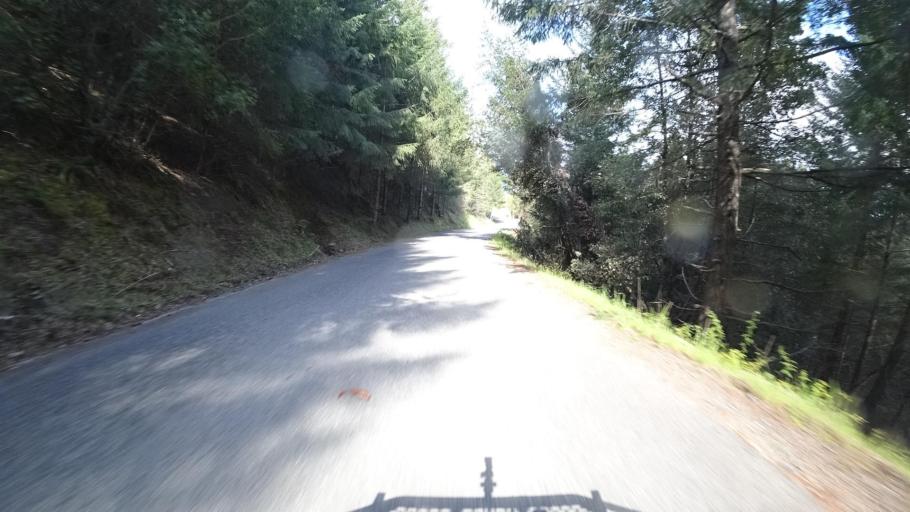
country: US
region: California
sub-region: Humboldt County
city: Redway
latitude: 40.1596
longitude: -123.5603
